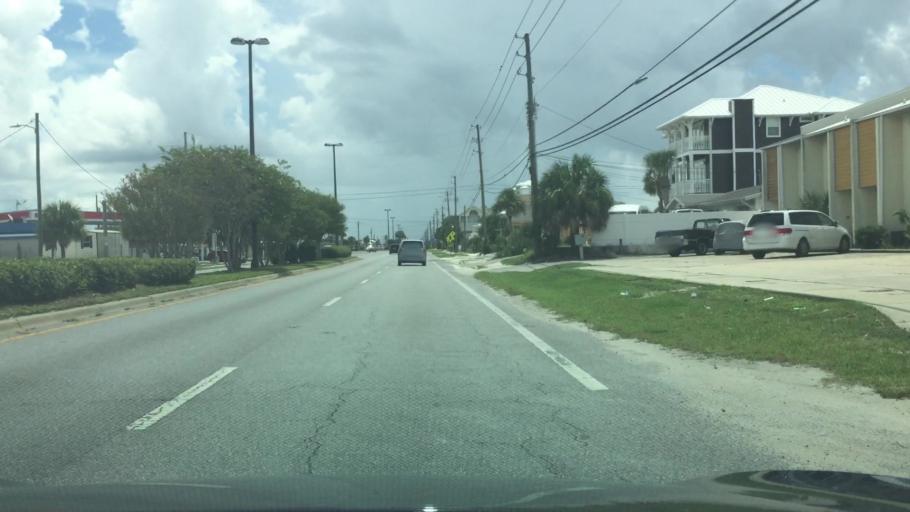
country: US
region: Florida
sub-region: Bay County
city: Panama City Beach
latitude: 30.1651
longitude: -85.7855
